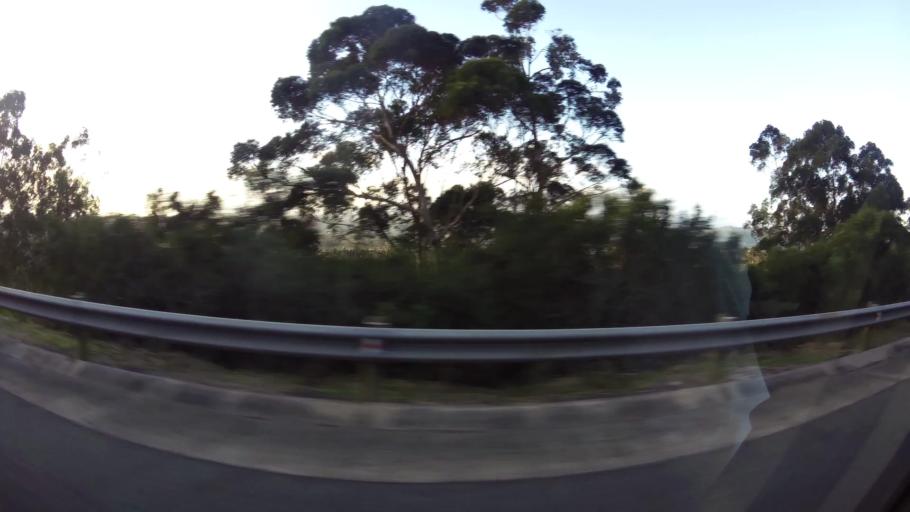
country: ZA
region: Western Cape
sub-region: Eden District Municipality
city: George
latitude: -34.0046
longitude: 22.7322
